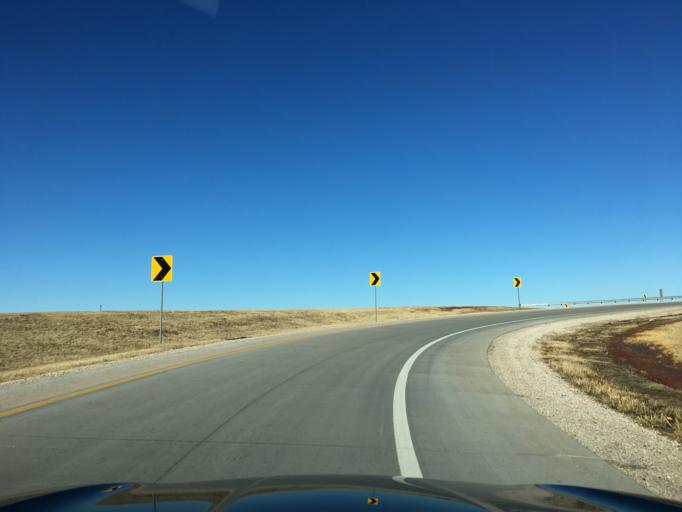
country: US
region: Oklahoma
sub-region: Noble County
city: Perry
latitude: 36.3991
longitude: -97.3285
